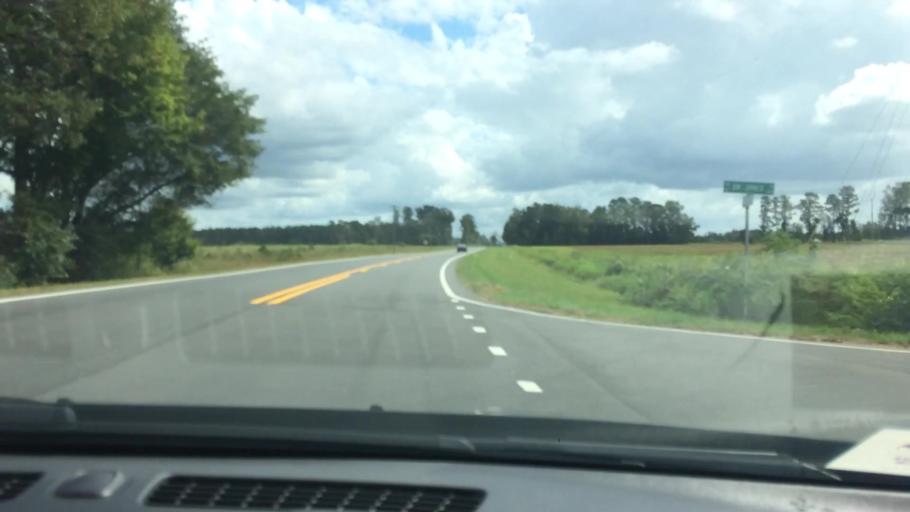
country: US
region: North Carolina
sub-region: Pitt County
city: Farmville
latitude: 35.5689
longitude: -77.5701
